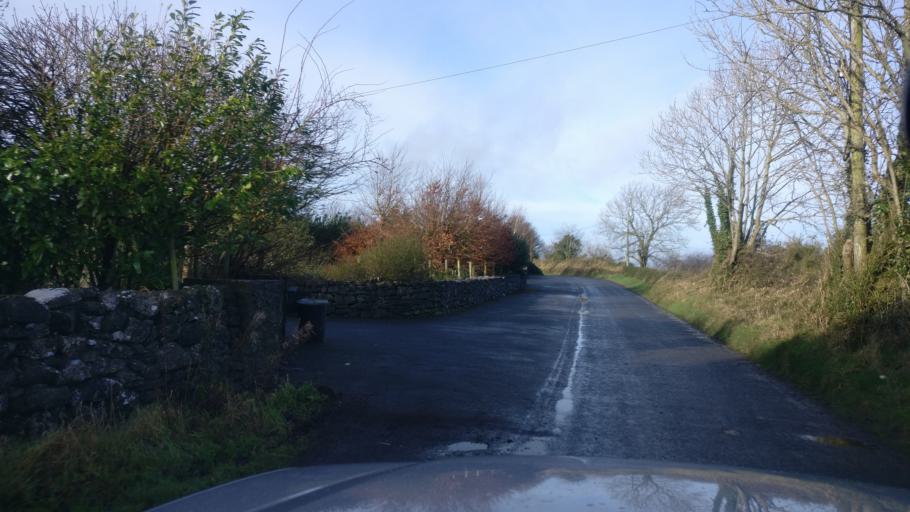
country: IE
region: Connaught
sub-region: County Galway
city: Loughrea
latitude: 53.1975
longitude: -8.6417
